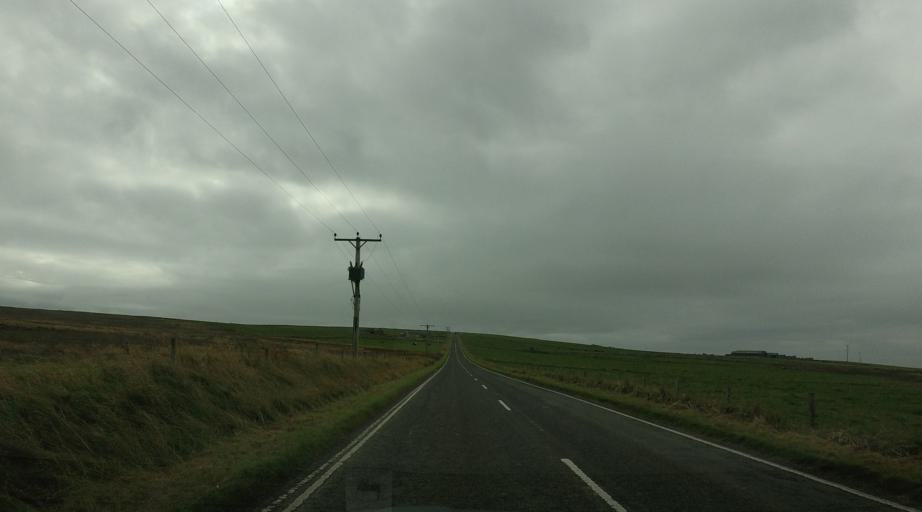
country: GB
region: Scotland
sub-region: Orkney Islands
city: Orkney
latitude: 58.7837
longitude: -2.9588
